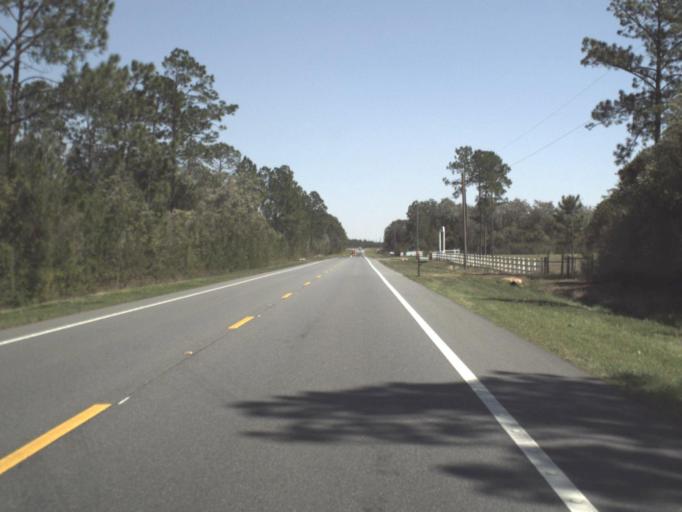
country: US
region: Florida
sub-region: Bay County
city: Youngstown
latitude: 30.4352
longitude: -85.3706
